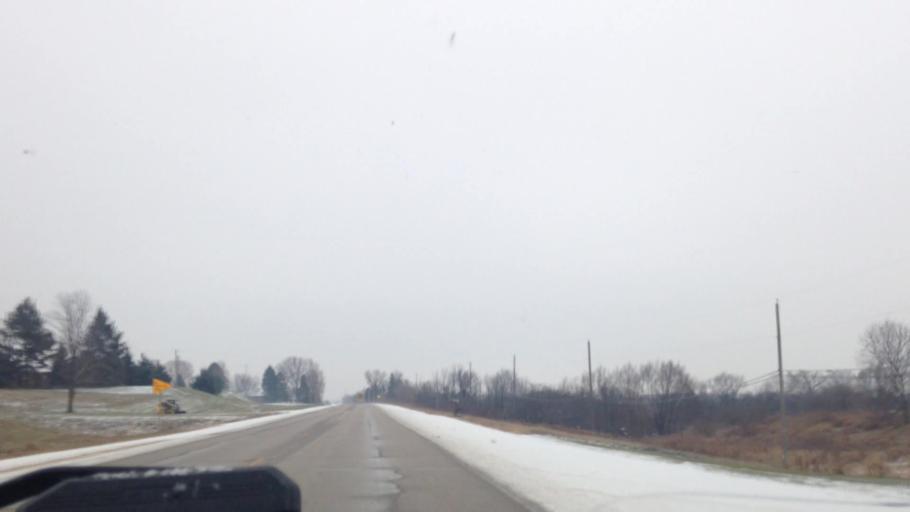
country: US
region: Wisconsin
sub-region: Dodge County
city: Mayville
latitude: 43.4313
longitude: -88.5421
